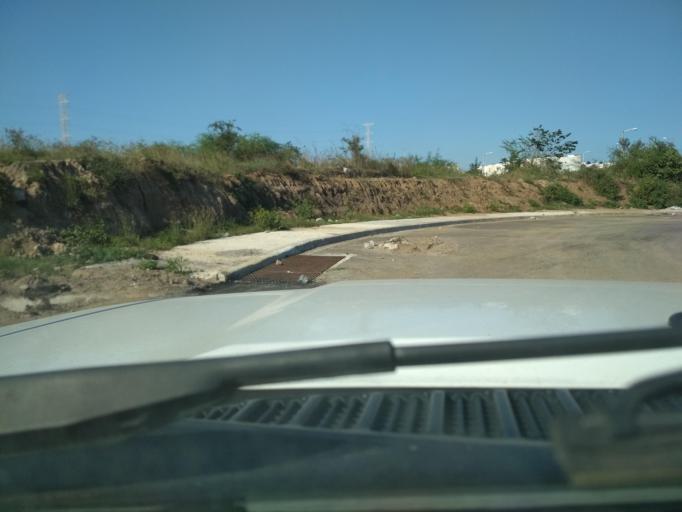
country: MX
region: Veracruz
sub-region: Veracruz
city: Las Amapolas
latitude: 19.1445
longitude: -96.2308
